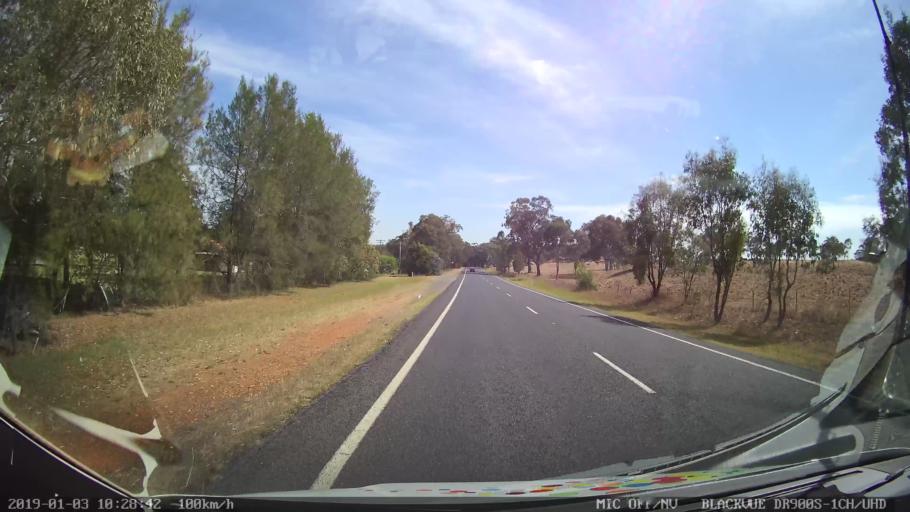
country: AU
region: New South Wales
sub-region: Young
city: Young
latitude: -34.3842
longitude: 148.2595
